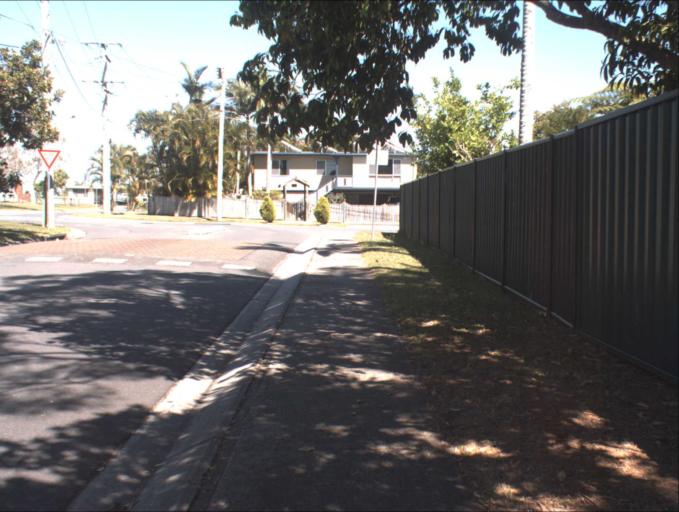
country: AU
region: Queensland
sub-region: Logan
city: Logan City
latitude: -27.6347
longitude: 153.1202
